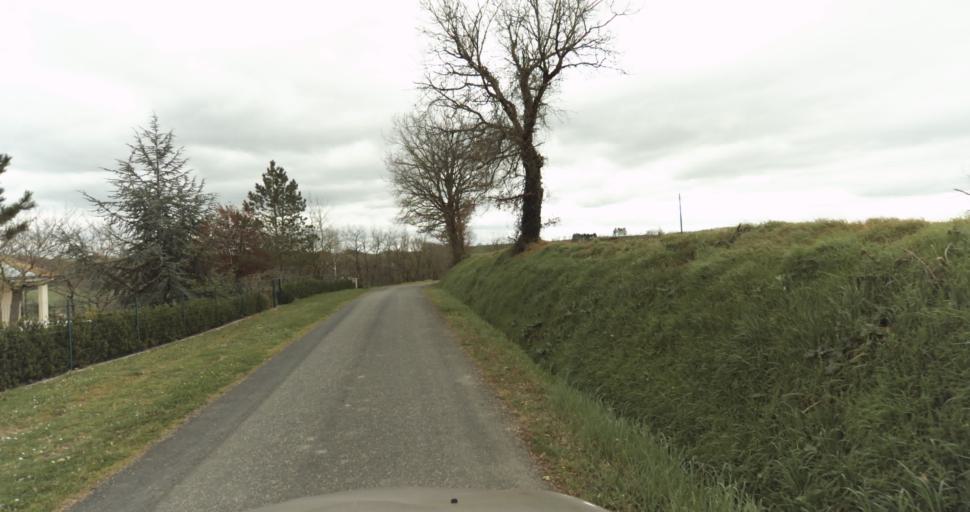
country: FR
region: Midi-Pyrenees
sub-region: Departement du Tarn
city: Puygouzon
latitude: 43.8708
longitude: 2.1693
